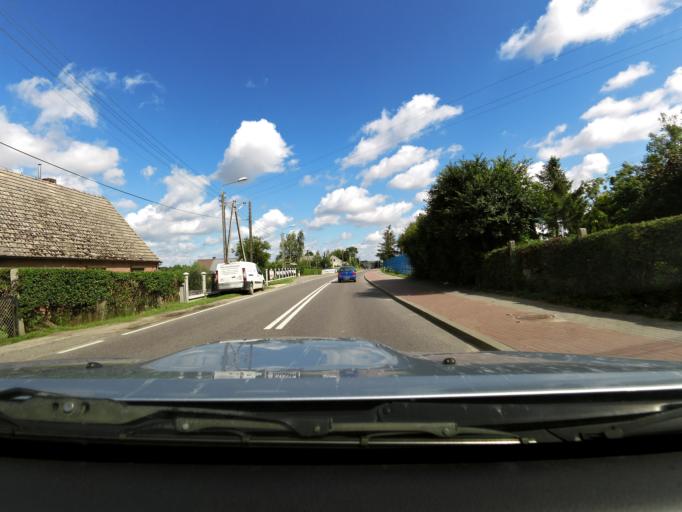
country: PL
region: Pomeranian Voivodeship
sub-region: Powiat kwidzynski
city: Kwidzyn
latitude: 53.7578
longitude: 18.9419
